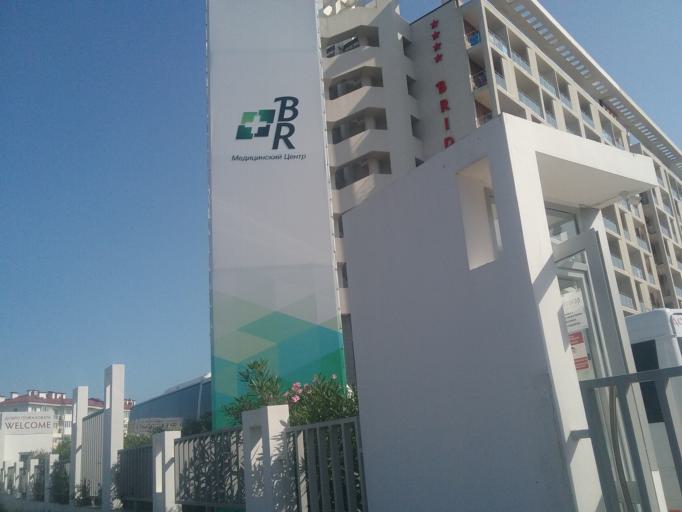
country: RU
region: Krasnodarskiy
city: Vysokoye
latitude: 43.3910
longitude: 39.9890
